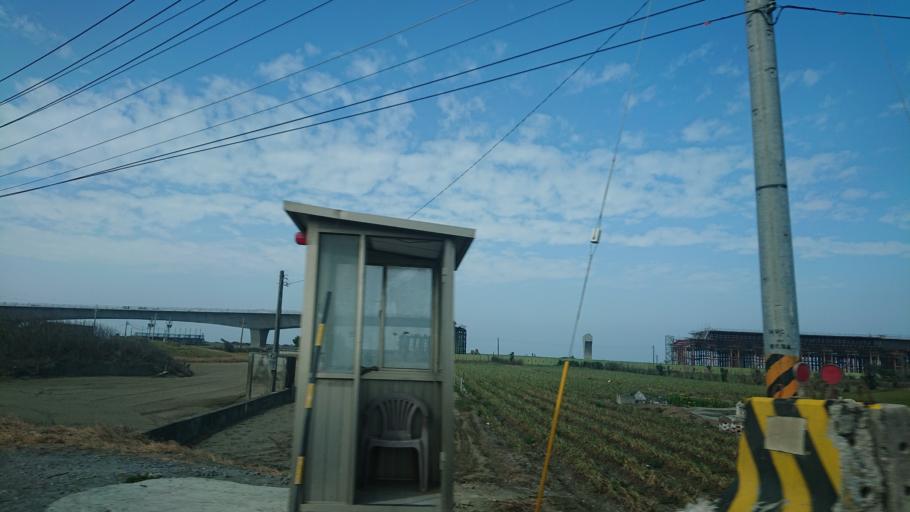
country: TW
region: Taiwan
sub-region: Changhua
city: Chang-hua
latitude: 23.9132
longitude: 120.3111
